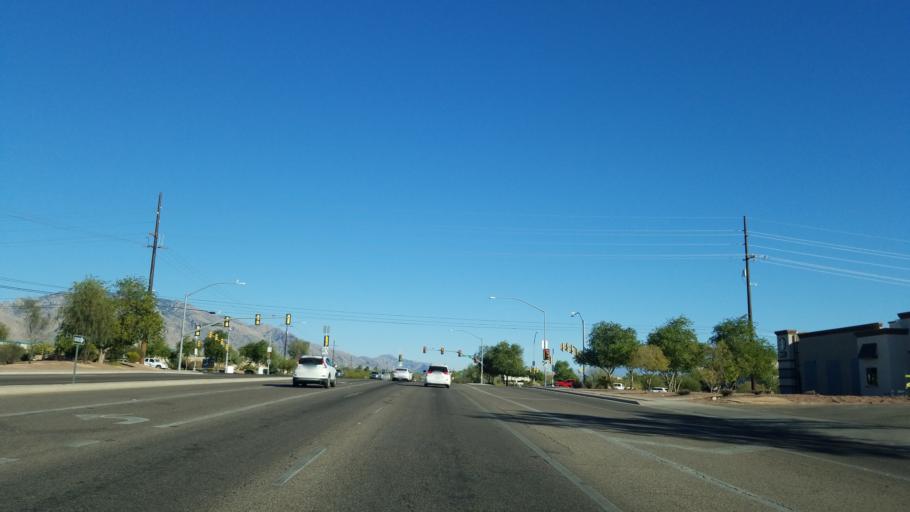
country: US
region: Arizona
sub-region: Pima County
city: Casas Adobes
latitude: 32.3231
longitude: -111.0136
